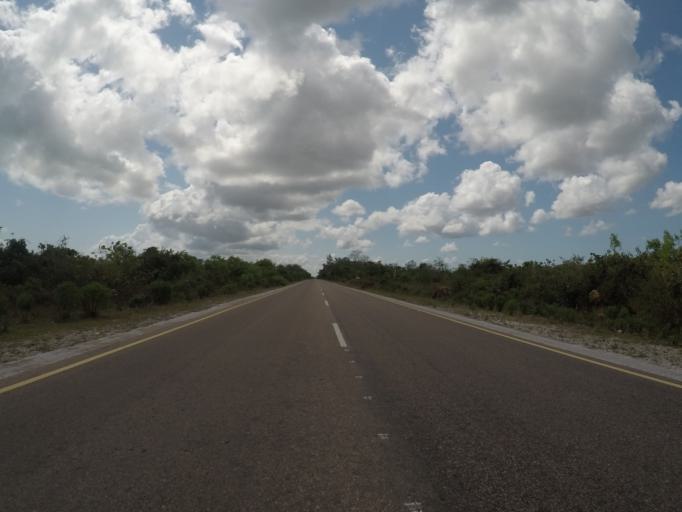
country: TZ
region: Zanzibar Central/South
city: Koani
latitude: -6.2639
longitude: 39.3602
